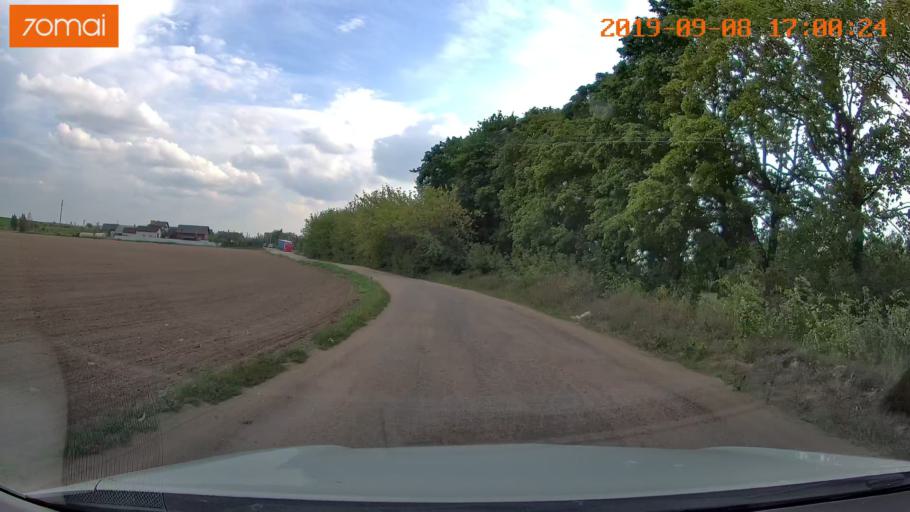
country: BY
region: Grodnenskaya
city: Hrodna
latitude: 53.7158
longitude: 23.9324
